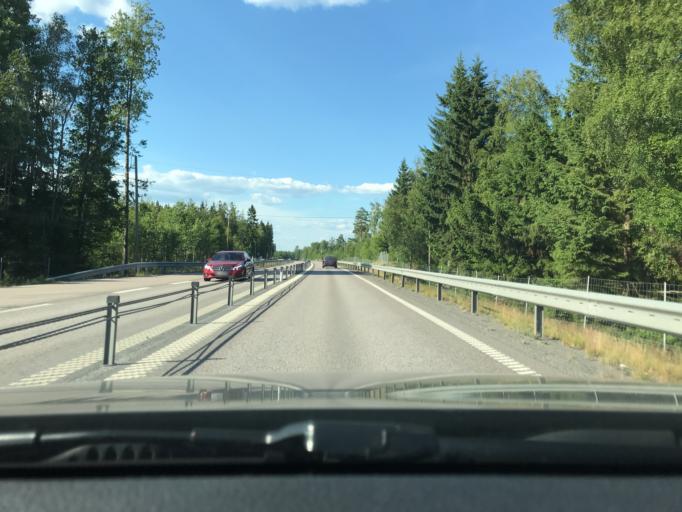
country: SE
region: Kronoberg
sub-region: Alvesta Kommun
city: Vislanda
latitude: 56.6741
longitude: 14.3137
